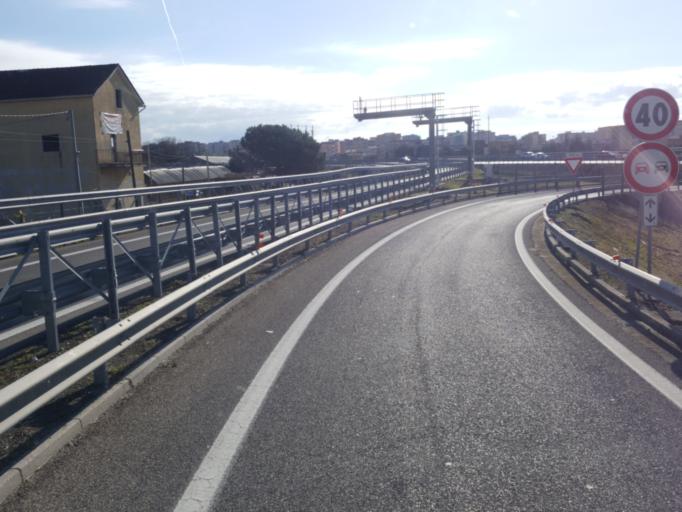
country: IT
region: Campania
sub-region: Provincia di Napoli
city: San Giorgio a Cremano
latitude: 40.8407
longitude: 14.3333
